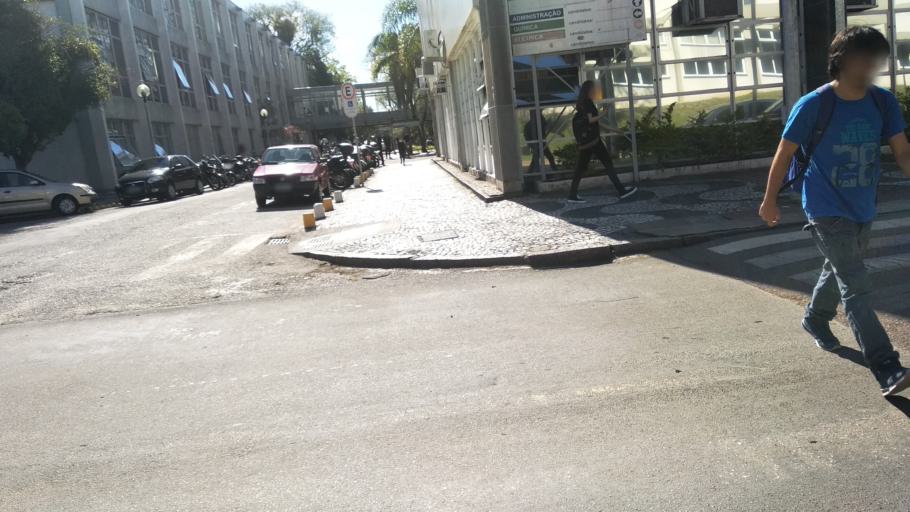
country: BR
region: Parana
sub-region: Pinhais
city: Pinhais
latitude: -25.4510
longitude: -49.2315
